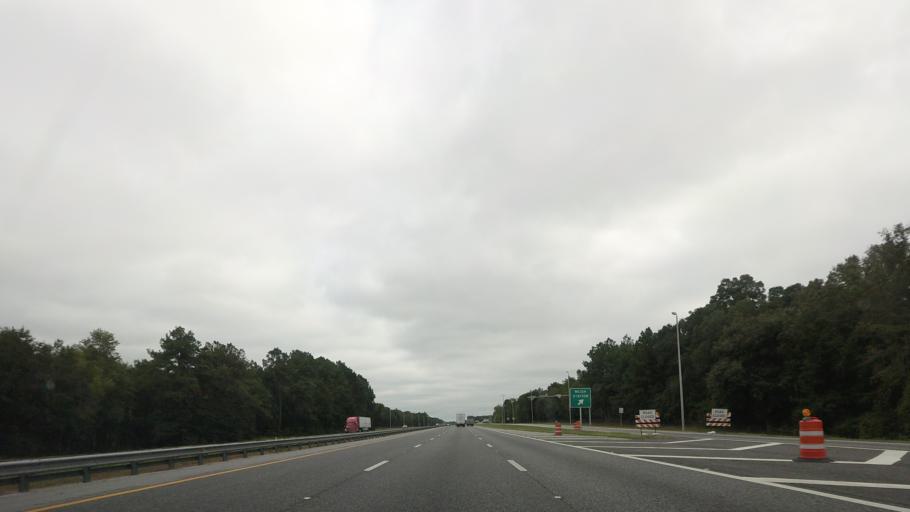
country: US
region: Florida
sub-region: Hamilton County
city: Jasper
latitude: 30.4290
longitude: -82.9084
